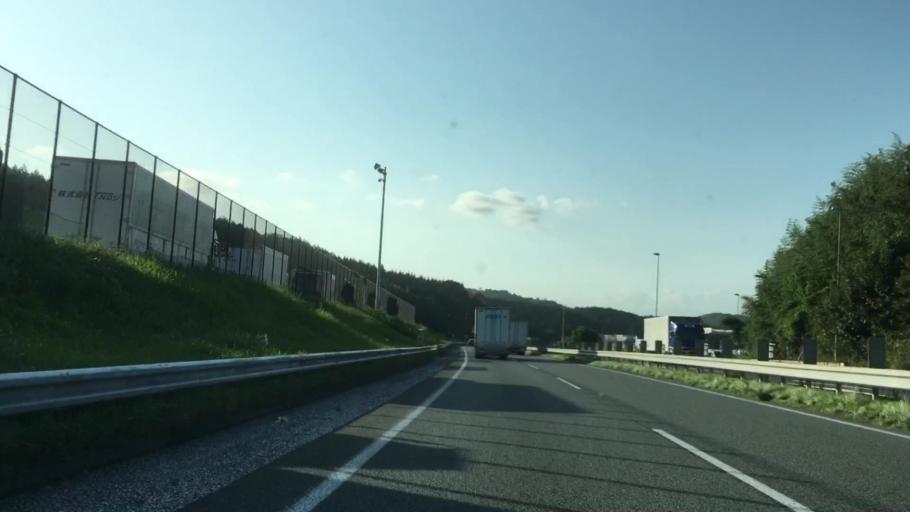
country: JP
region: Yamaguchi
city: Ogori-shimogo
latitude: 34.1529
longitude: 131.3389
